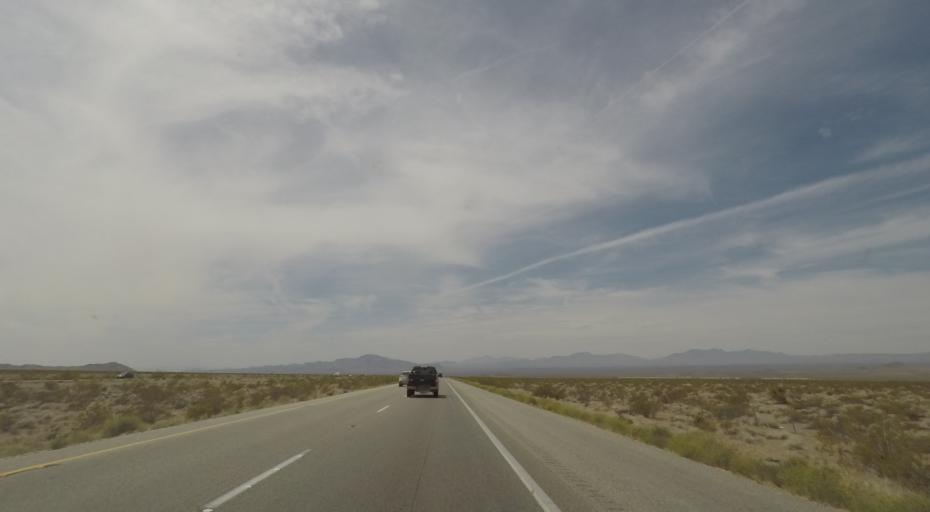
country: US
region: California
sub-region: San Bernardino County
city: Needles
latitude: 34.8238
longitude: -115.0999
